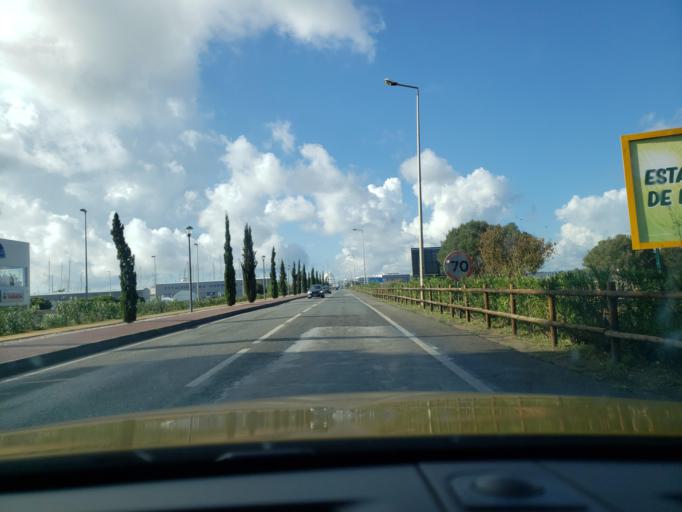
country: PT
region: Faro
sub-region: Portimao
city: Portimao
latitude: 37.1368
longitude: -8.5249
